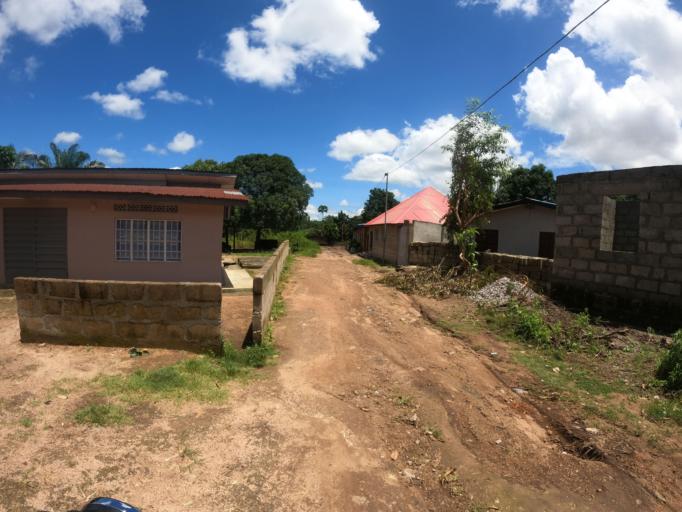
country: SL
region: Northern Province
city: Makeni
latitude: 8.8951
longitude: -12.0630
